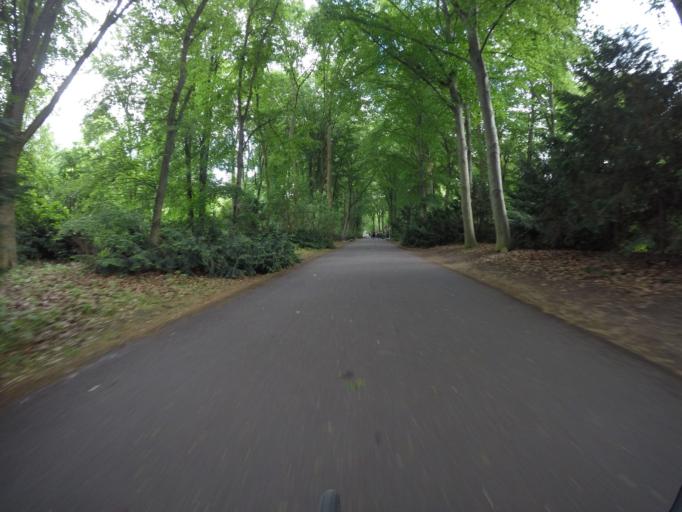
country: DE
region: Berlin
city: Tiergarten Bezirk
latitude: 52.5150
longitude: 13.3634
